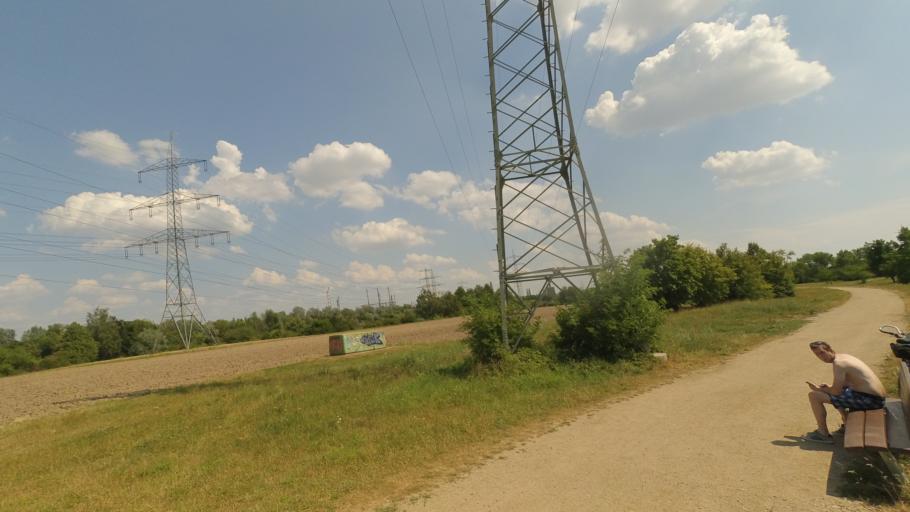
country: DE
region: Rheinland-Pfalz
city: Frankenthal
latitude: 49.5322
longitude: 8.3979
